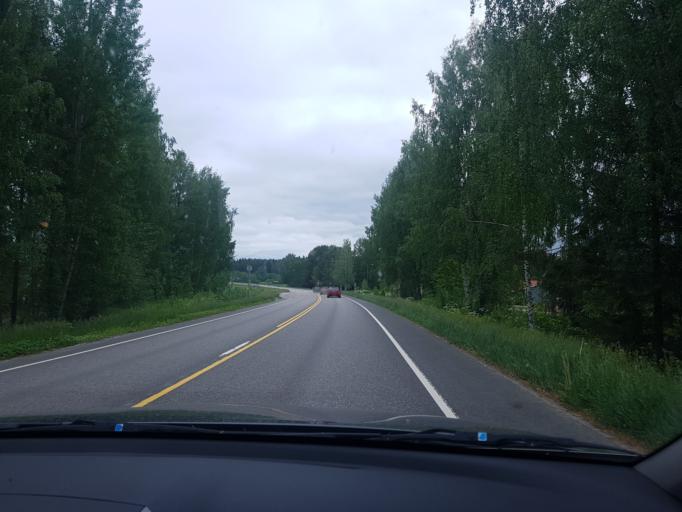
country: FI
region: Pirkanmaa
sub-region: Tampere
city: Paelkaene
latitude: 61.2616
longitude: 24.3543
